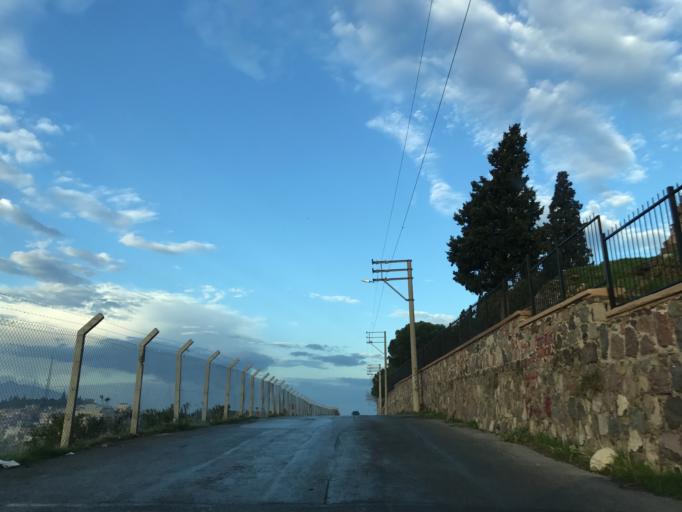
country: TR
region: Izmir
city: Izmir
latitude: 38.4126
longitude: 27.1472
